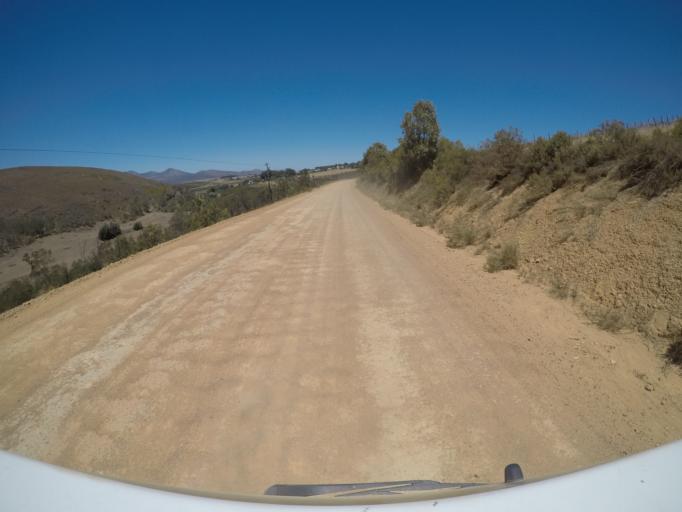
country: ZA
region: Western Cape
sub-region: Overberg District Municipality
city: Grabouw
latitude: -34.2156
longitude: 19.2095
